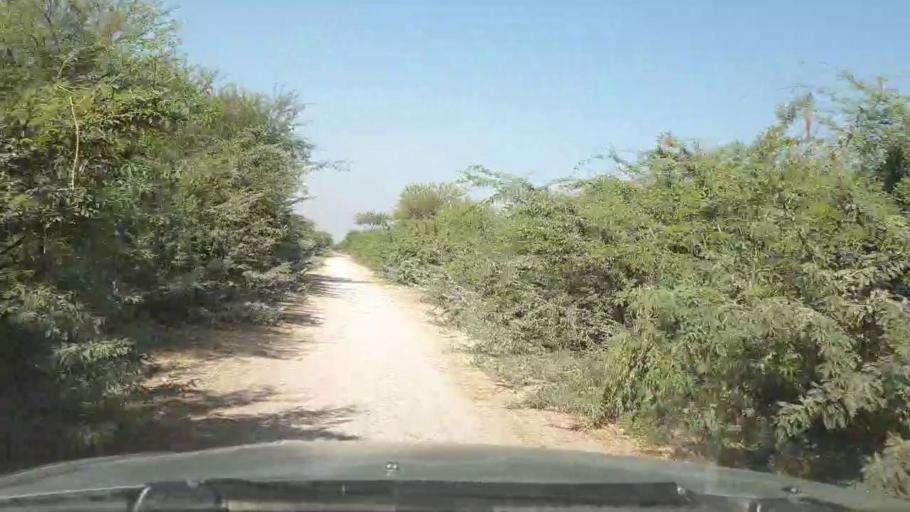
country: PK
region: Sindh
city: Kario
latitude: 24.9097
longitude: 68.5349
